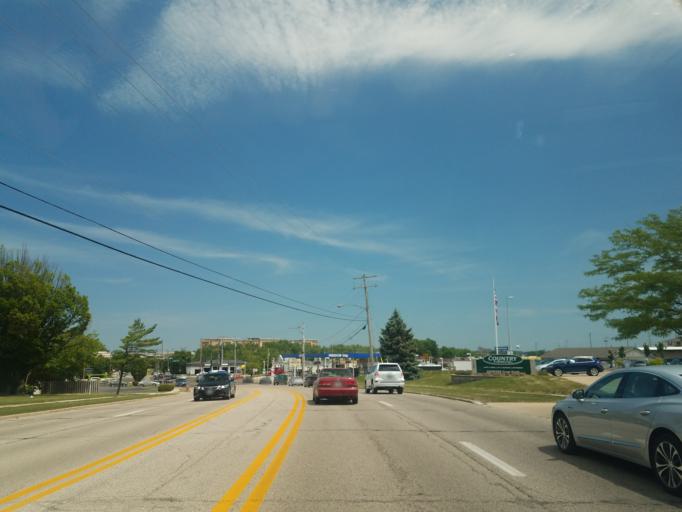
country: US
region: Illinois
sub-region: McLean County
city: Normal
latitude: 40.5008
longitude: -88.9578
